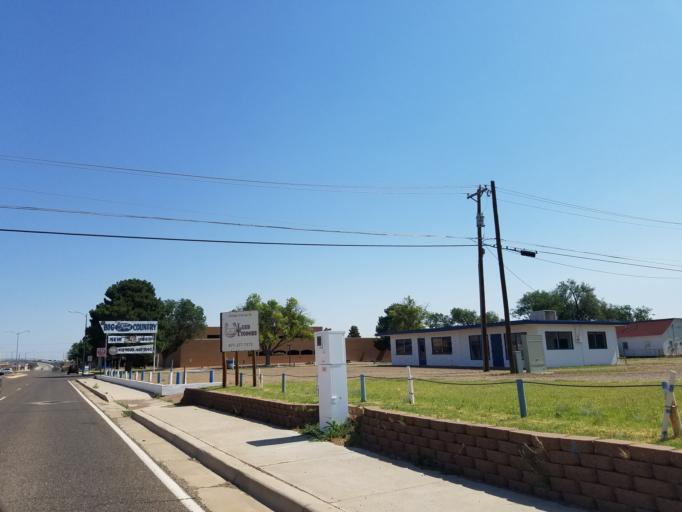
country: US
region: New Mexico
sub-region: Quay County
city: Tucumcari
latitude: 35.1749
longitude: -103.7248
